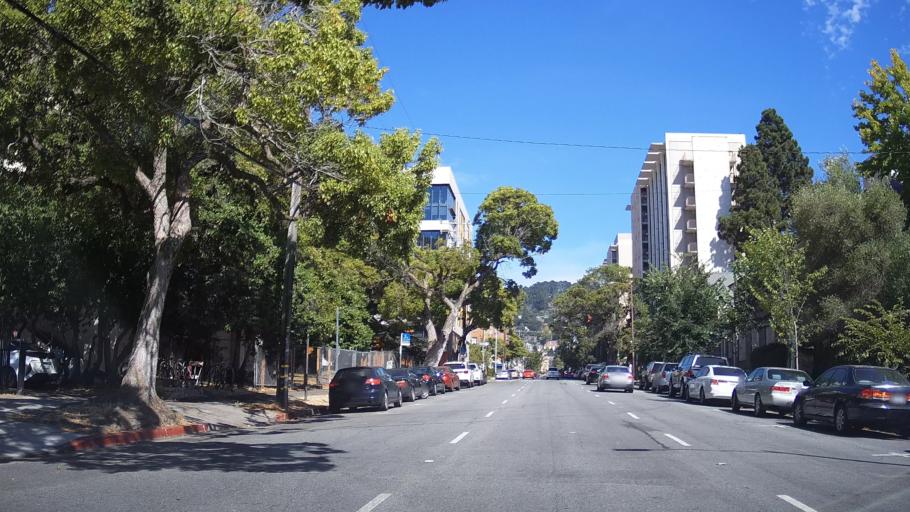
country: US
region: California
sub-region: Alameda County
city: Berkeley
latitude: 37.8674
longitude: -122.2623
